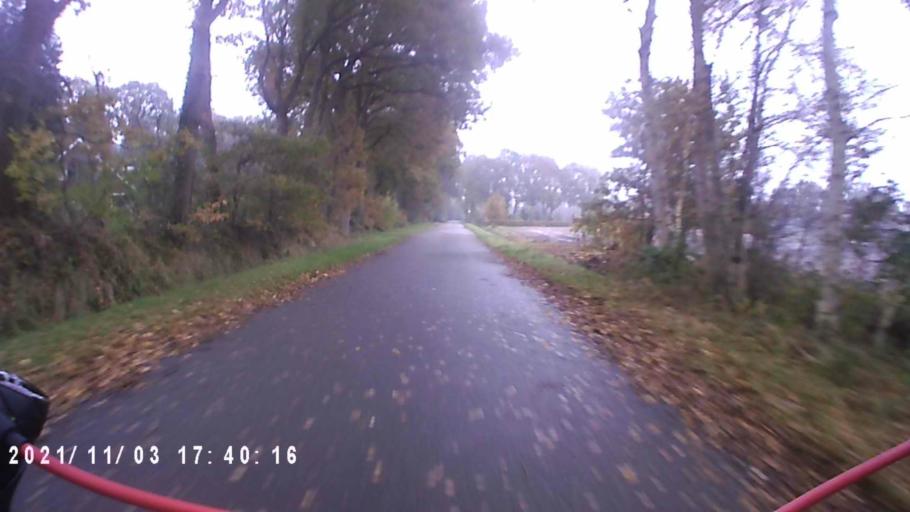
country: NL
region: Drenthe
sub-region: Gemeente Westerveld
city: Dwingeloo
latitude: 52.8657
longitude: 6.2988
